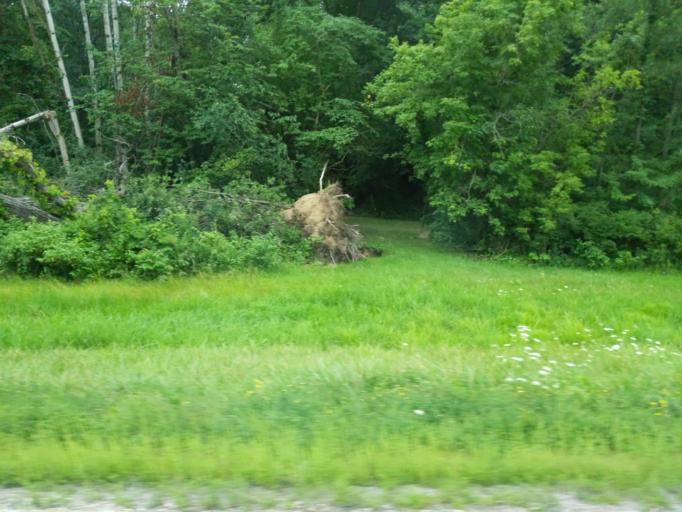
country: US
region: Wisconsin
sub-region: Sauk County
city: Sauk City
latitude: 43.2351
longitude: -89.7351
